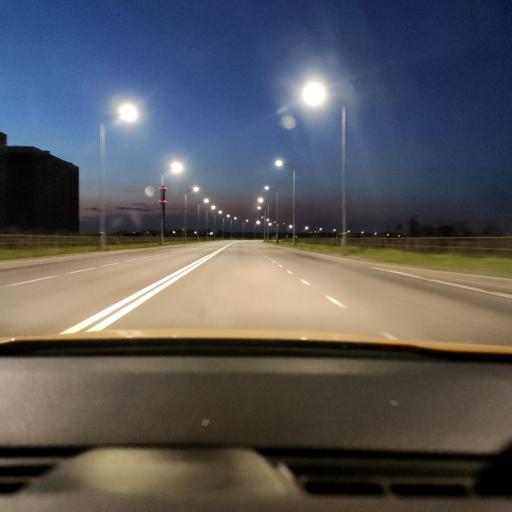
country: RU
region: Moskovskaya
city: Shcherbinka
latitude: 55.4986
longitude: 37.5234
